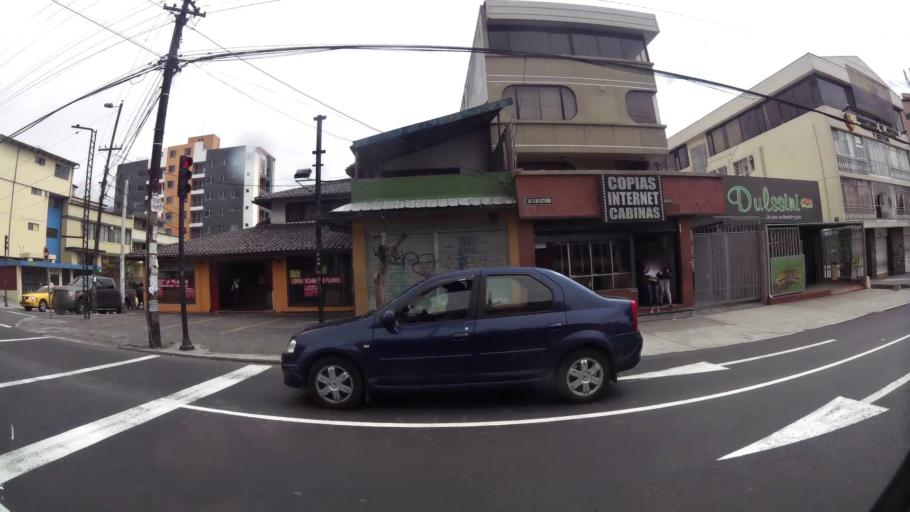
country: EC
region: Pichincha
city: Quito
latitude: -0.2072
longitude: -78.4891
